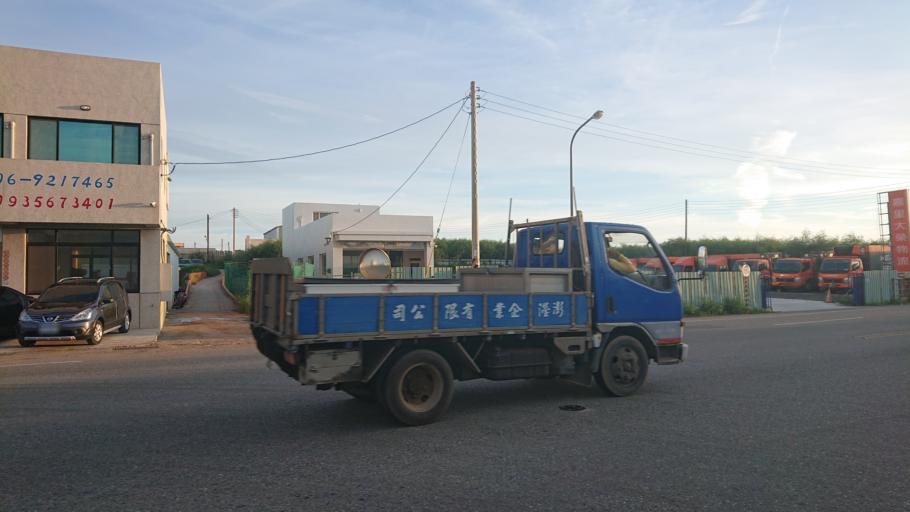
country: TW
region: Taiwan
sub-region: Penghu
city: Ma-kung
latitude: 23.5691
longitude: 119.5920
